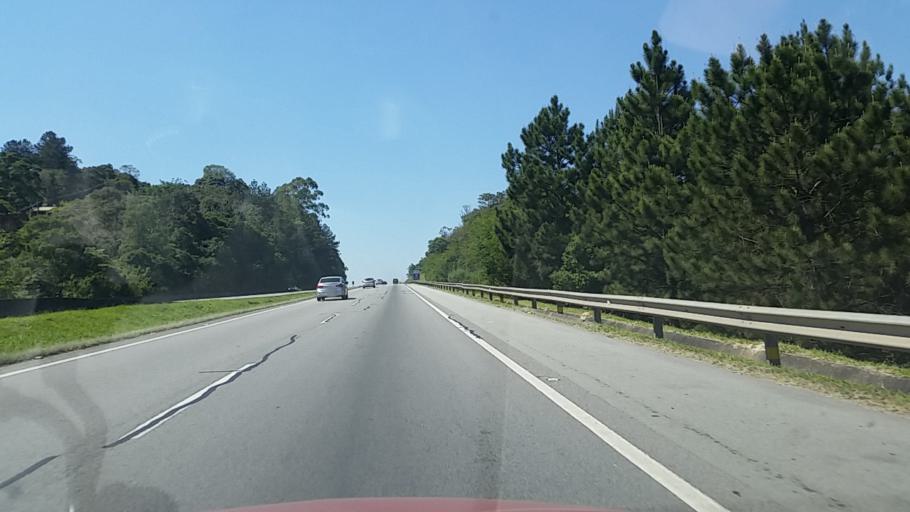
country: BR
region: Sao Paulo
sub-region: Juquitiba
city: Juquitiba
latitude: -23.9662
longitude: -47.1299
